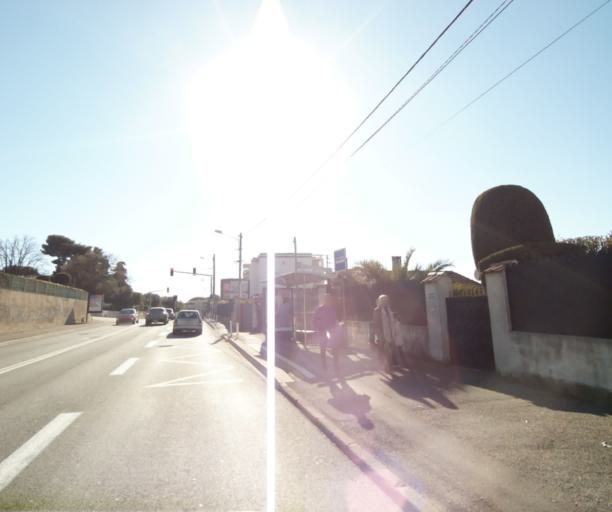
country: FR
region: Provence-Alpes-Cote d'Azur
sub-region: Departement des Alpes-Maritimes
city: Biot
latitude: 43.5967
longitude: 7.1053
